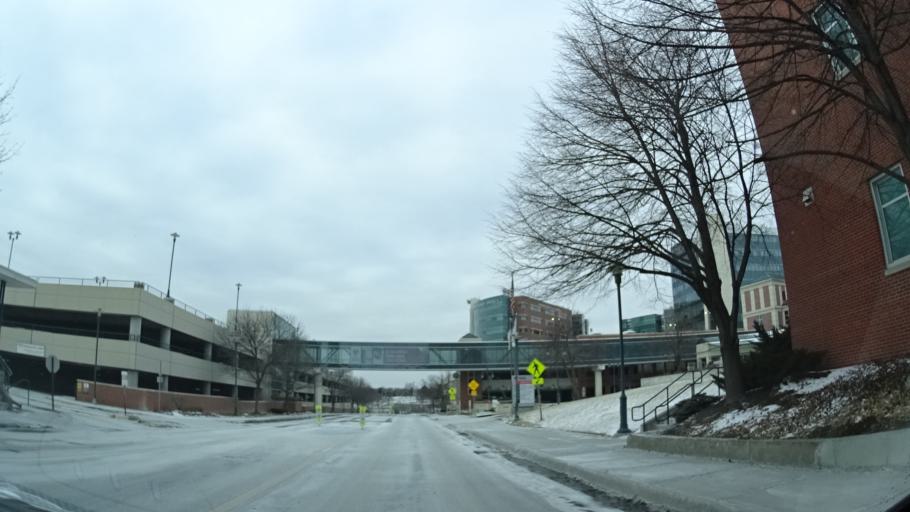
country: US
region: Nebraska
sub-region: Douglas County
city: Omaha
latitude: 41.2543
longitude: -95.9782
